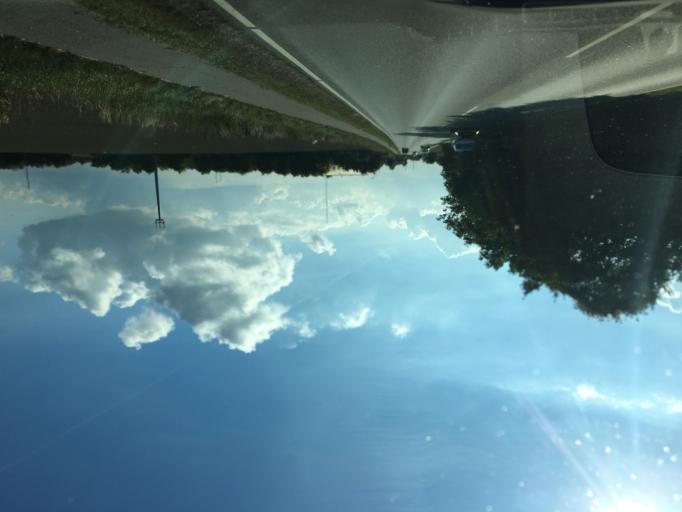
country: DK
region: South Denmark
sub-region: Fredericia Kommune
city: Snoghoj
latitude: 55.5643
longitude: 9.6814
